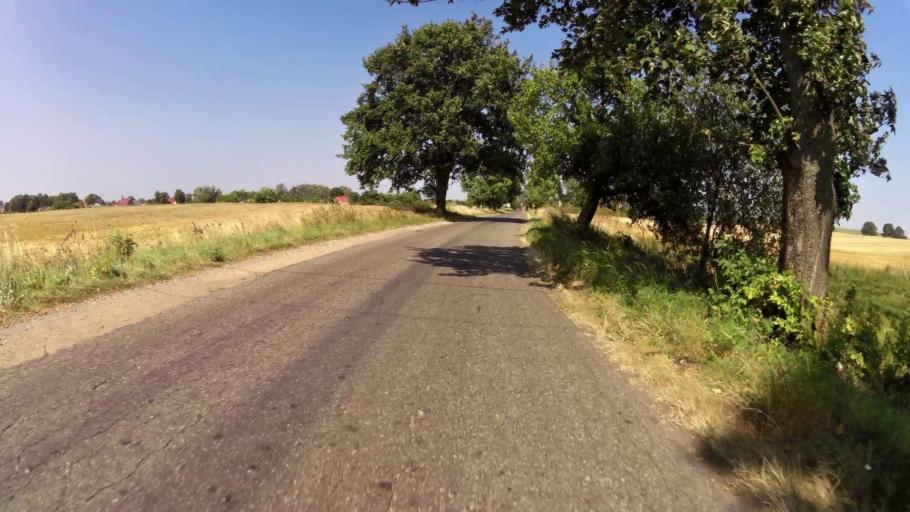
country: PL
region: West Pomeranian Voivodeship
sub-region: Powiat walecki
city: Walcz
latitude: 53.2259
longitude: 16.4653
